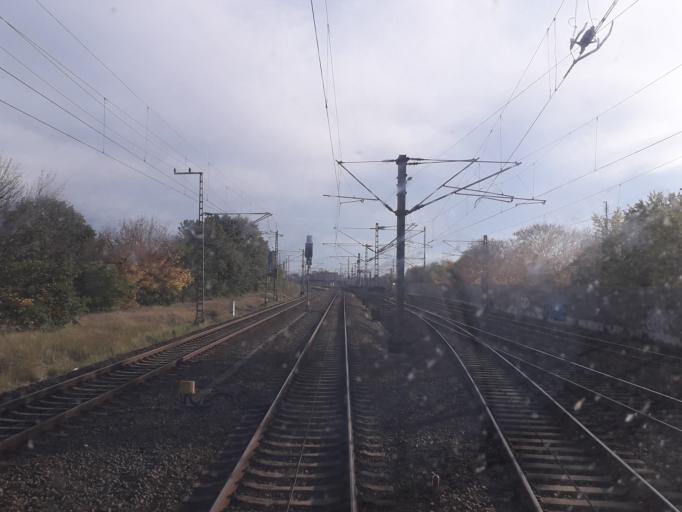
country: DE
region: Brandenburg
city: Wittenberge
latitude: 53.0100
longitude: 11.7615
